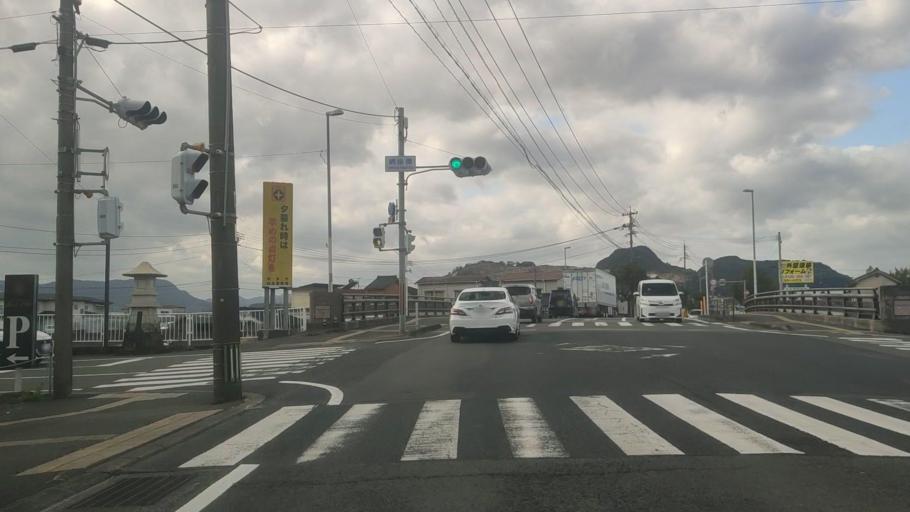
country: JP
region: Kagoshima
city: Kajiki
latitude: 31.7357
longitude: 130.6643
